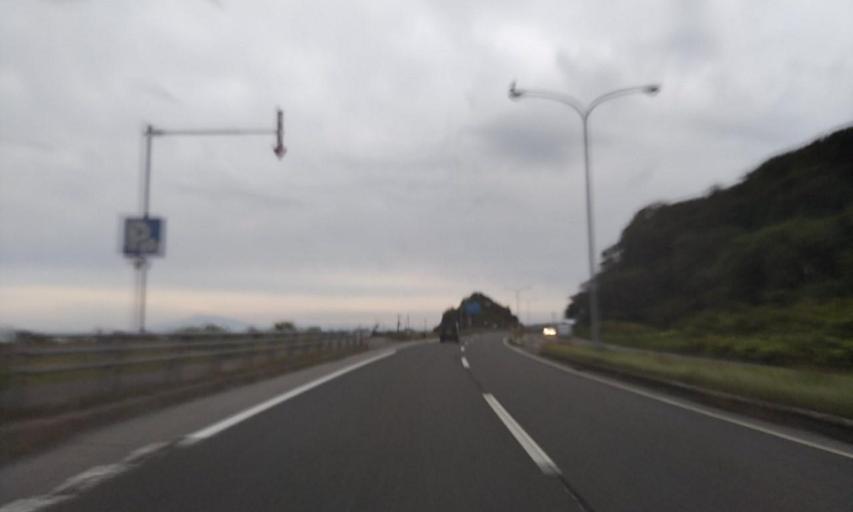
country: JP
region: Hokkaido
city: Abashiri
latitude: 43.9937
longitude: 144.2963
